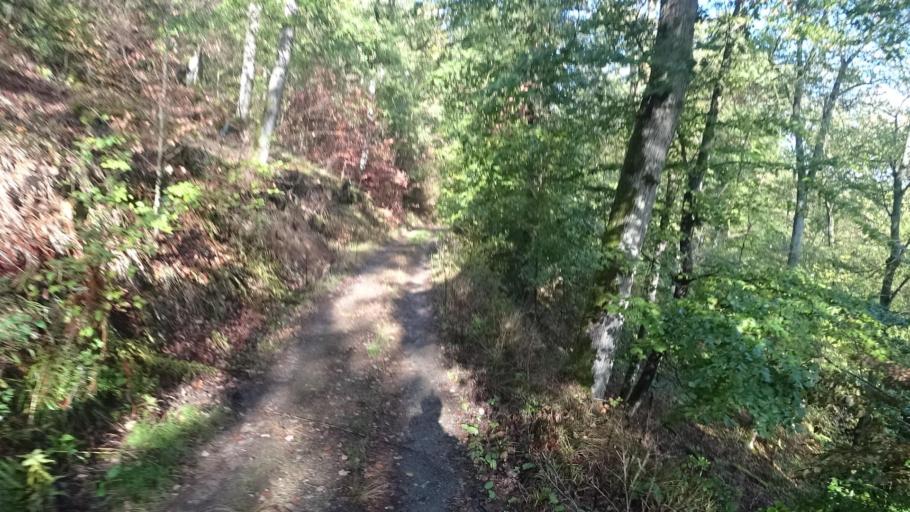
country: DE
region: Rheinland-Pfalz
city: Kamp-Bornhofen
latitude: 50.2045
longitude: 7.6031
